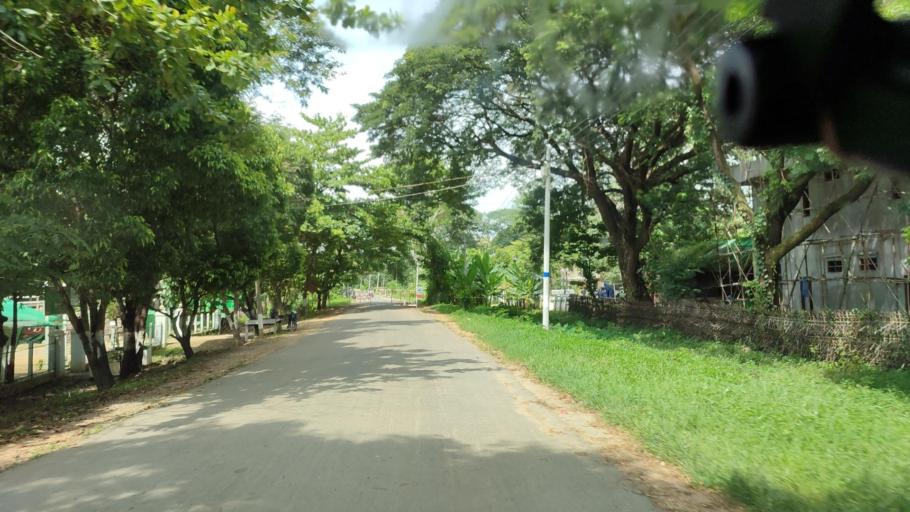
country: MM
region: Bago
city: Pyay
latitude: 18.7174
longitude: 95.1586
